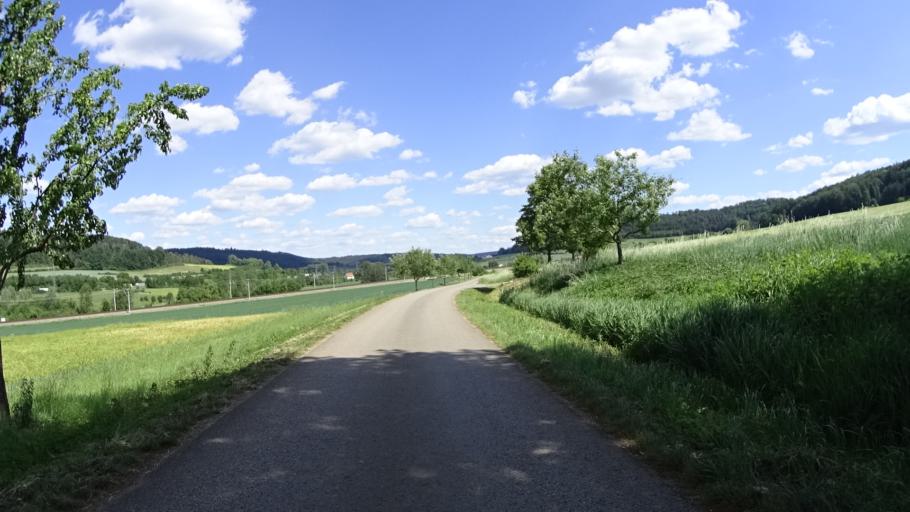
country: DE
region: Bavaria
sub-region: Regierungsbezirk Mittelfranken
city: Greding
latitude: 49.0691
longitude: 11.2972
